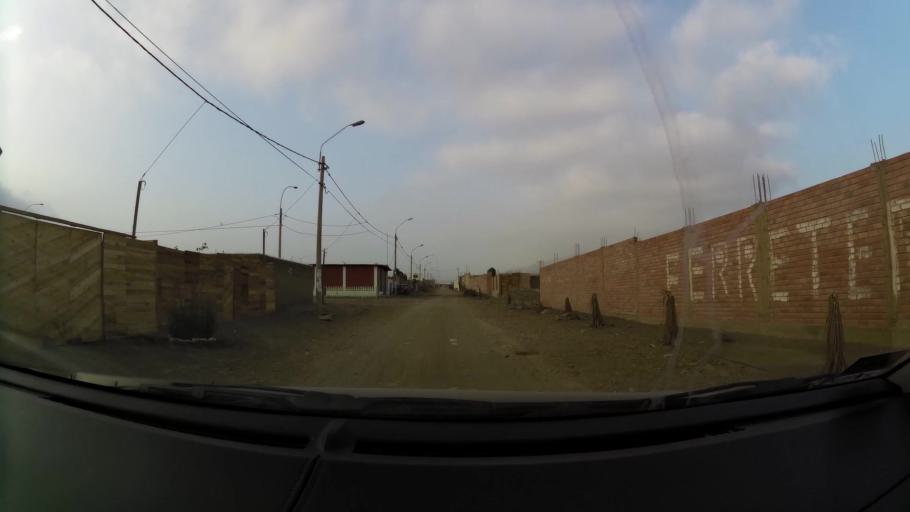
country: PE
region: Lima
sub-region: Lima
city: Santa Rosa
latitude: -11.7416
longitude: -77.1407
